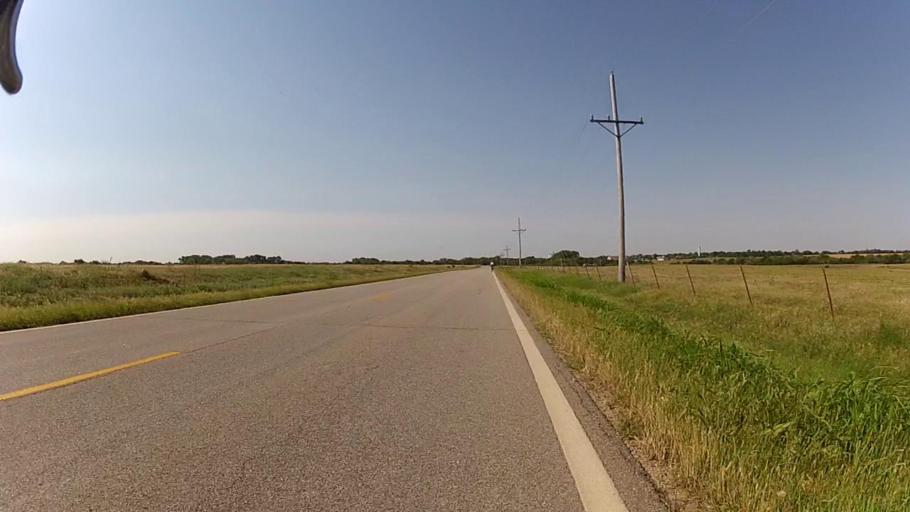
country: US
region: Kansas
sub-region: Sumner County
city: Caldwell
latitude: 37.0511
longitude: -97.6010
